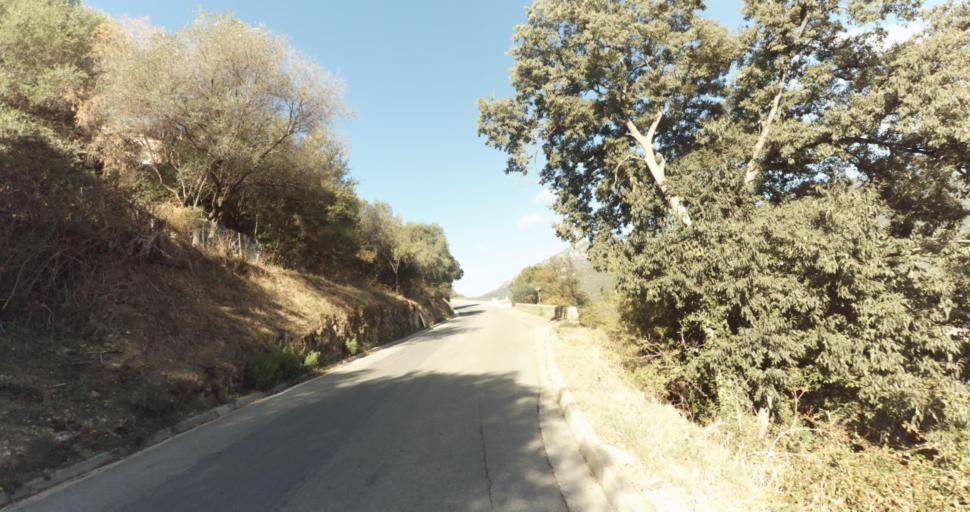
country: FR
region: Corsica
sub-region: Departement de la Corse-du-Sud
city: Ajaccio
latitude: 41.9250
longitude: 8.7269
